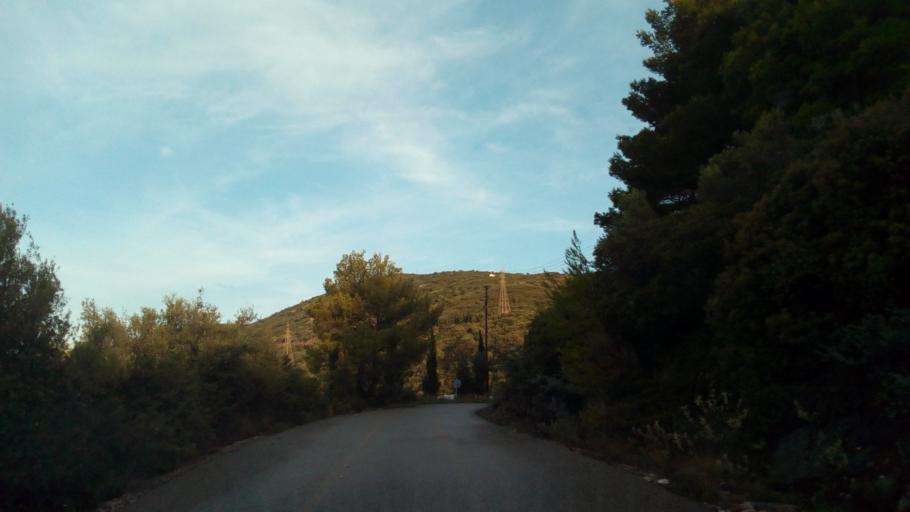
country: GR
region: West Greece
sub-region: Nomos Aitolias kai Akarnanias
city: Nafpaktos
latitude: 38.3992
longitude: 21.8352
